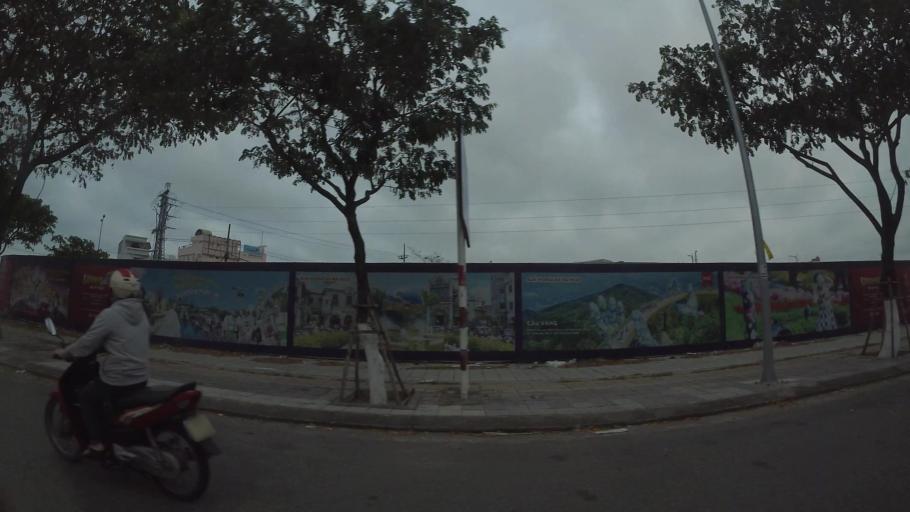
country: VN
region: Da Nang
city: Son Tra
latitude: 16.0525
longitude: 108.2365
